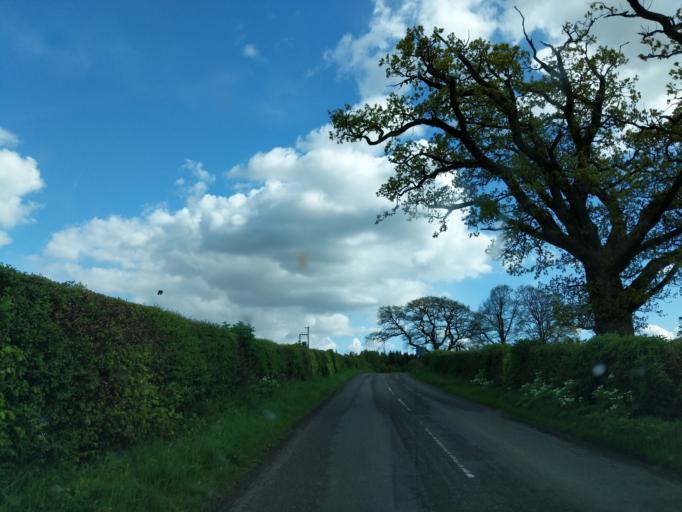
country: GB
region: Scotland
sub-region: Stirling
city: Callander
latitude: 56.1663
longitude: -4.2649
